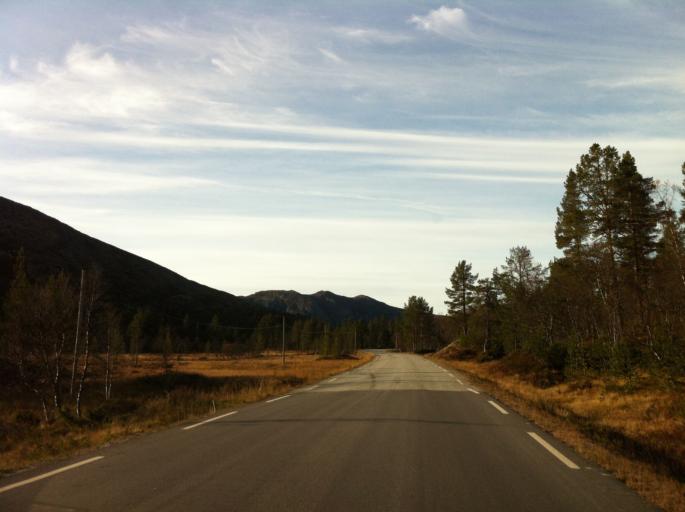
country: NO
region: Hedmark
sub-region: Engerdal
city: Engerdal
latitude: 62.0842
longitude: 12.0710
